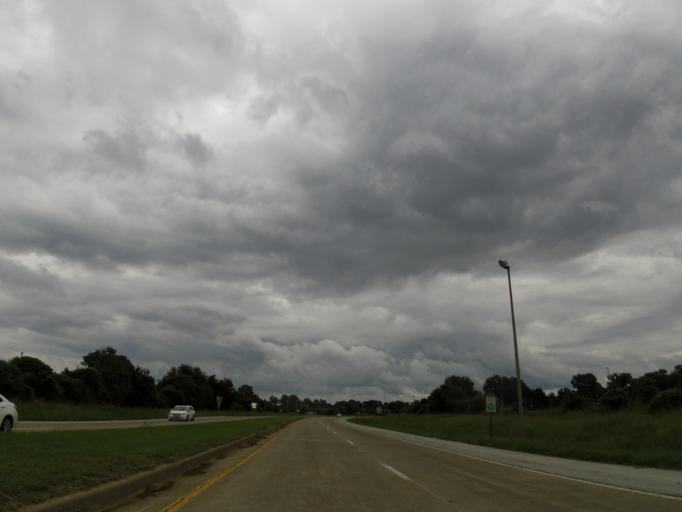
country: US
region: Illinois
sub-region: Alexander County
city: Cairo
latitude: 37.0419
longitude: -89.1980
